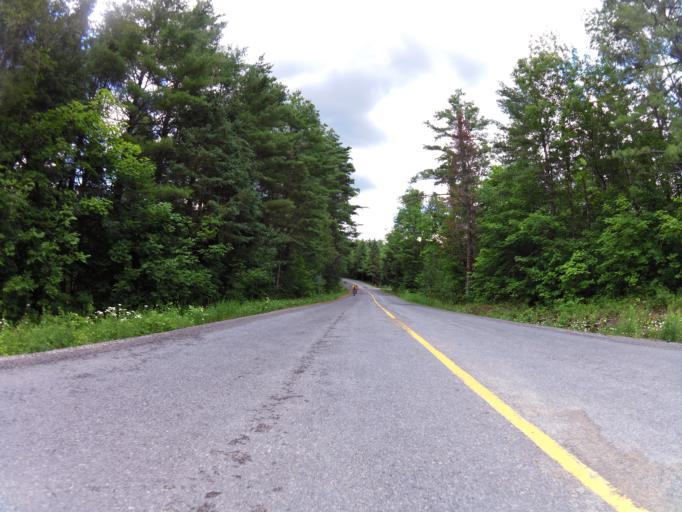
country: CA
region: Ontario
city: Renfrew
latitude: 45.0477
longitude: -76.6943
